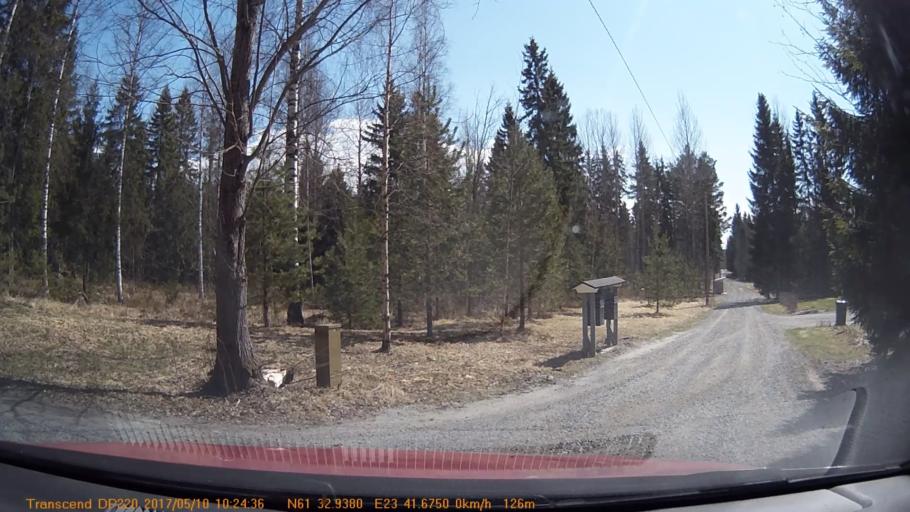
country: FI
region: Pirkanmaa
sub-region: Tampere
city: Yloejaervi
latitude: 61.5489
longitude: 23.6946
